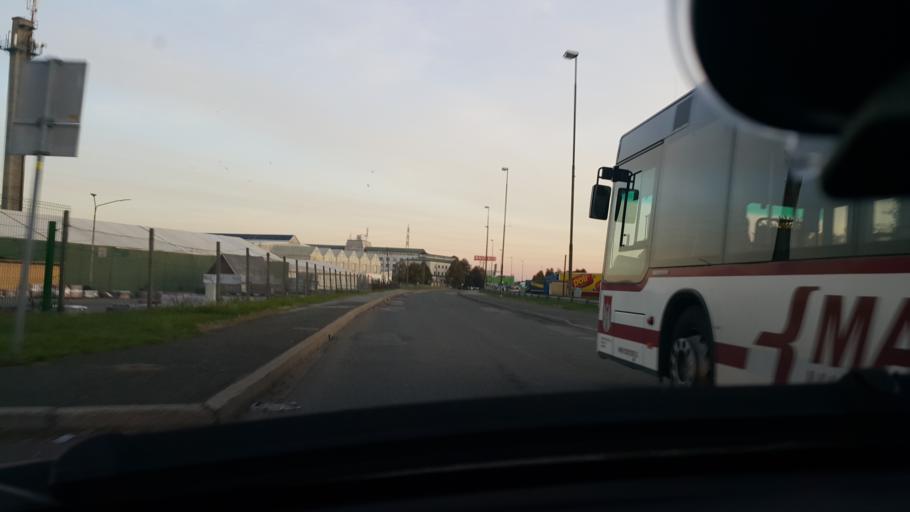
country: SI
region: Maribor
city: Razvanje
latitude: 46.5285
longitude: 15.6473
